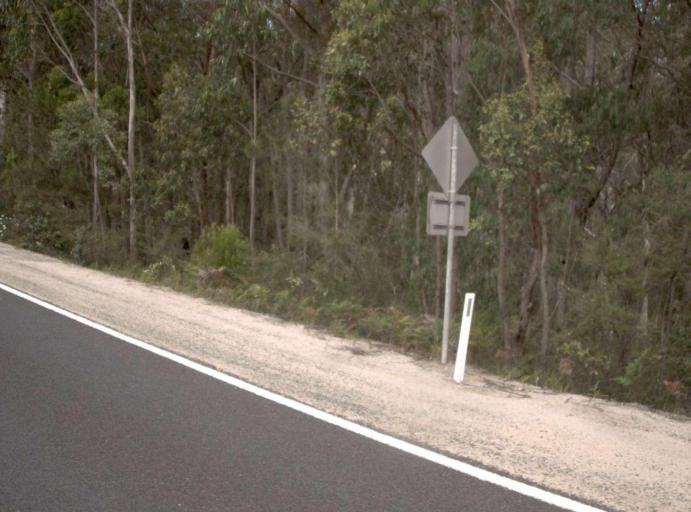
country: AU
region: New South Wales
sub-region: Bega Valley
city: Eden
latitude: -37.3967
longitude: 149.6739
